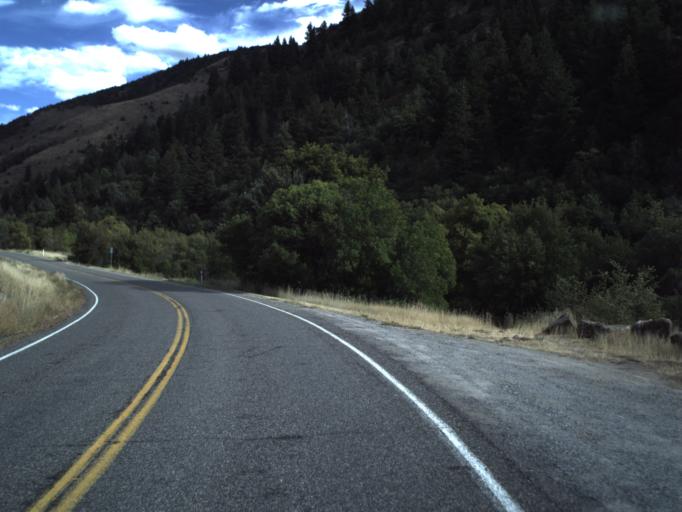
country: US
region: Utah
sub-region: Cache County
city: Millville
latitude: 41.6099
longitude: -111.6270
